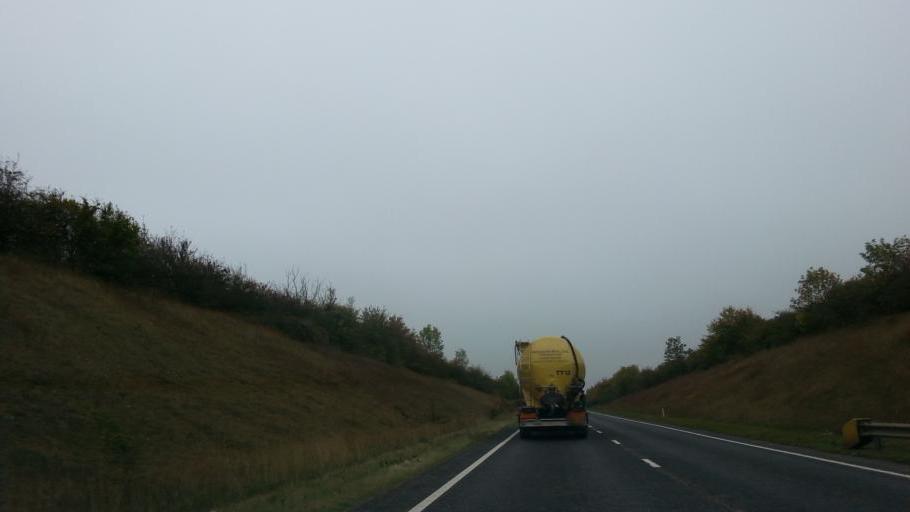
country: GB
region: England
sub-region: Northamptonshire
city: Thrapston
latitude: 52.3802
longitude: -0.5243
